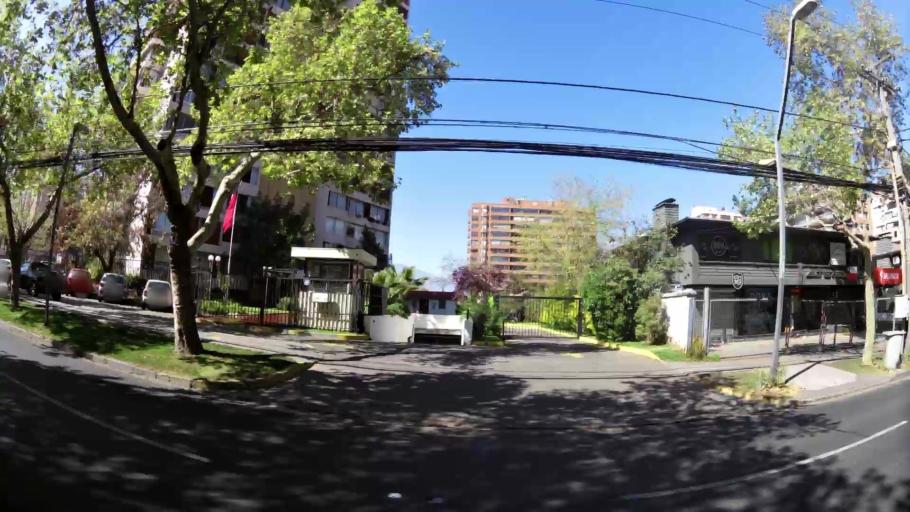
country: CL
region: Santiago Metropolitan
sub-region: Provincia de Santiago
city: Villa Presidente Frei, Nunoa, Santiago, Chile
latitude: -33.4172
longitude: -70.5667
